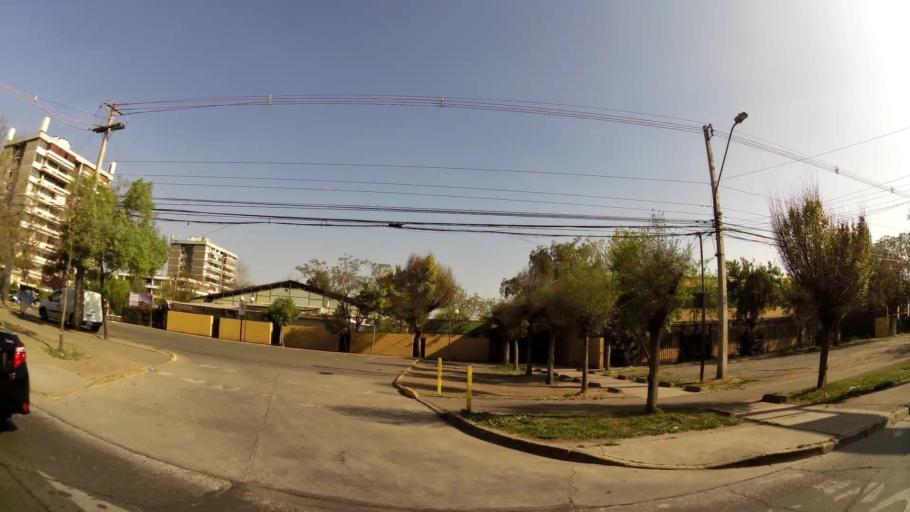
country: CL
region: Santiago Metropolitan
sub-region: Provincia de Santiago
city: Villa Presidente Frei, Nunoa, Santiago, Chile
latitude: -33.4590
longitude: -70.5809
